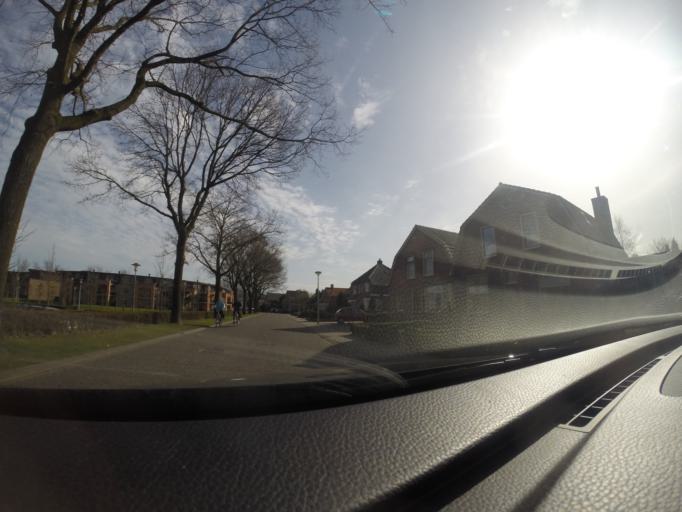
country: NL
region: Gelderland
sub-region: Berkelland
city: Eibergen
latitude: 52.0395
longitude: 6.6142
